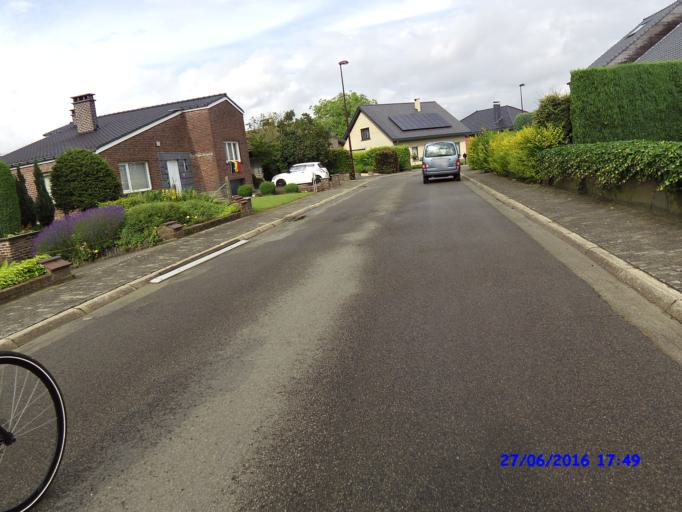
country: BE
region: Flanders
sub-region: Provincie Vlaams-Brabant
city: Liedekerke
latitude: 50.8773
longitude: 4.1197
